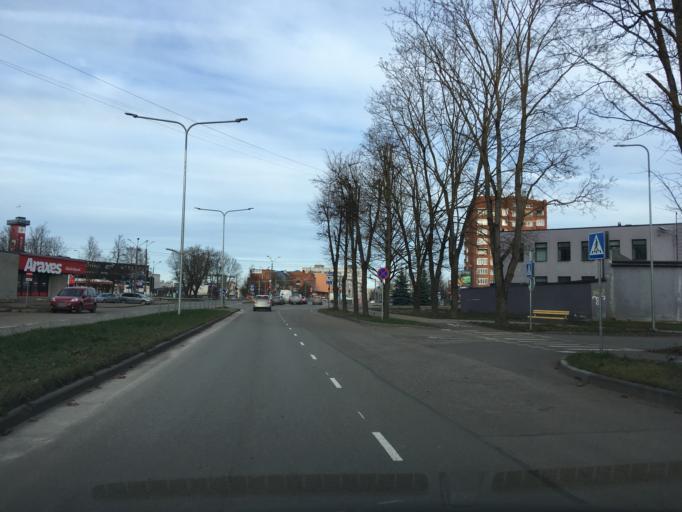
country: EE
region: Ida-Virumaa
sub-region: Narva linn
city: Narva
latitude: 59.3784
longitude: 28.1799
